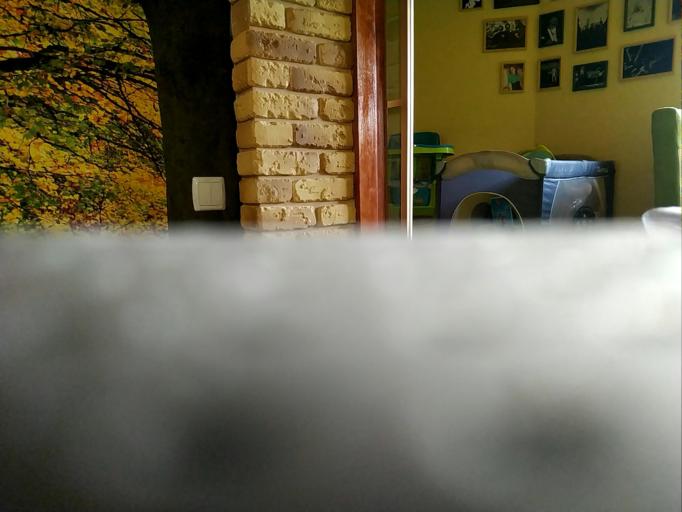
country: RU
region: Kaluga
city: Seredeyskiy
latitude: 54.0113
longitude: 35.3131
